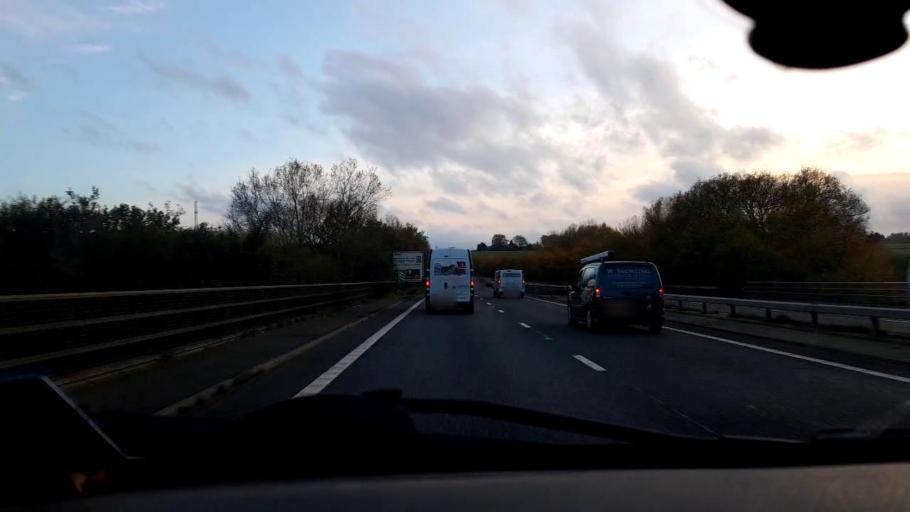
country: GB
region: England
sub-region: Norfolk
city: Bowthorpe
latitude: 52.6329
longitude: 1.1959
